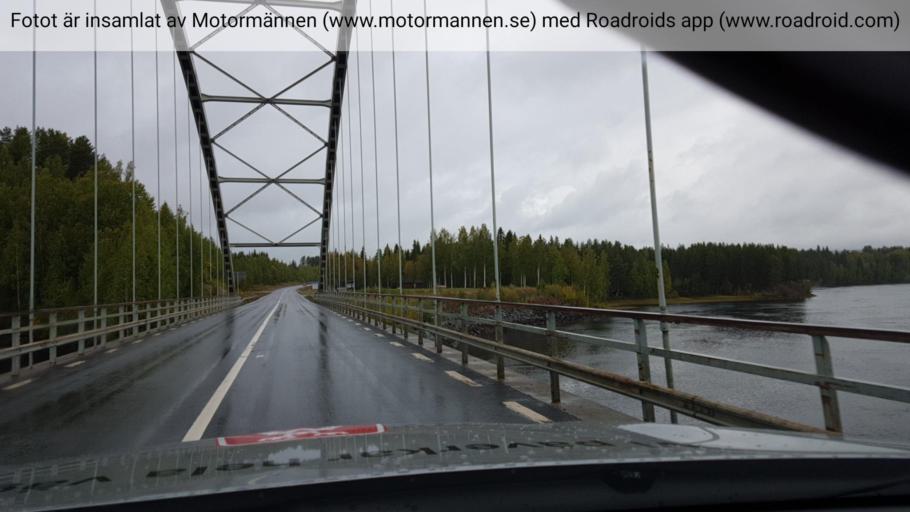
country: SE
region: Norrbotten
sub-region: Alvsbyns Kommun
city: AElvsbyn
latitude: 66.2313
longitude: 20.8711
